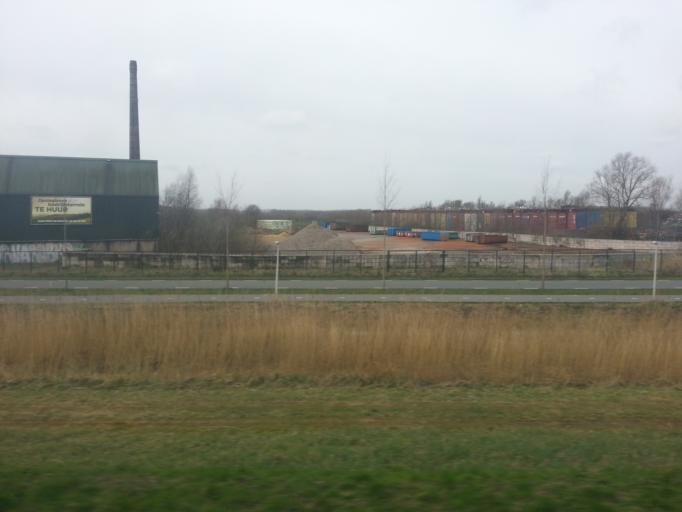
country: NL
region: Gelderland
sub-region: Gemeente Culemborg
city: Culemborg
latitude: 51.9316
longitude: 5.2400
